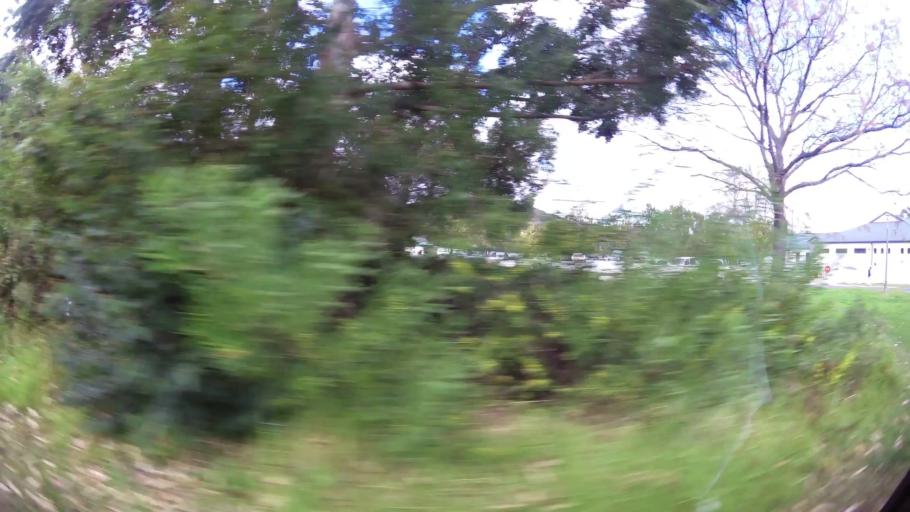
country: ZA
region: Western Cape
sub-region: Eden District Municipality
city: Knysna
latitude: -34.0578
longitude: 23.0790
